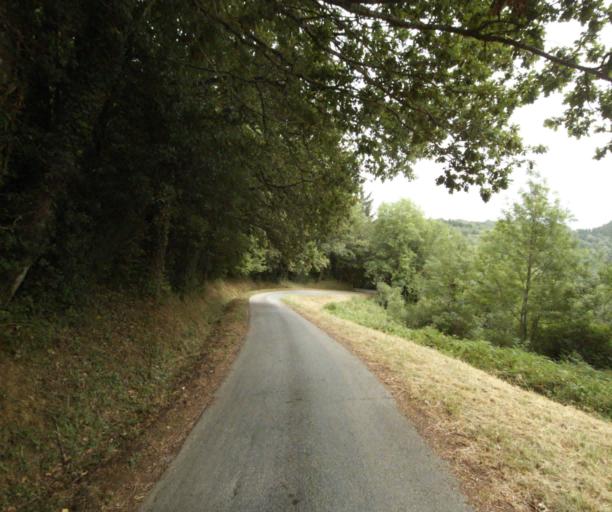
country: FR
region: Midi-Pyrenees
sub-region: Departement du Tarn
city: Soreze
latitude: 43.4135
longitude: 2.0864
